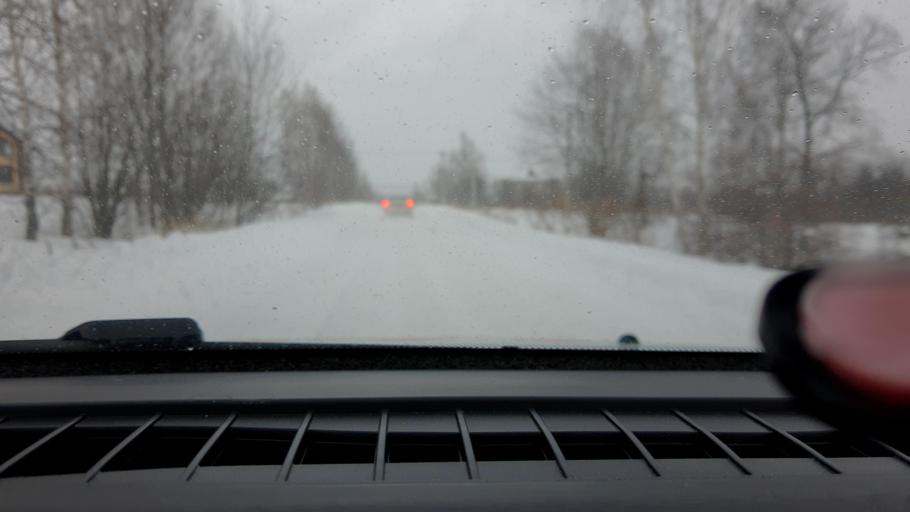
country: RU
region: Nizjnij Novgorod
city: Burevestnik
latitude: 56.1514
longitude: 43.7546
